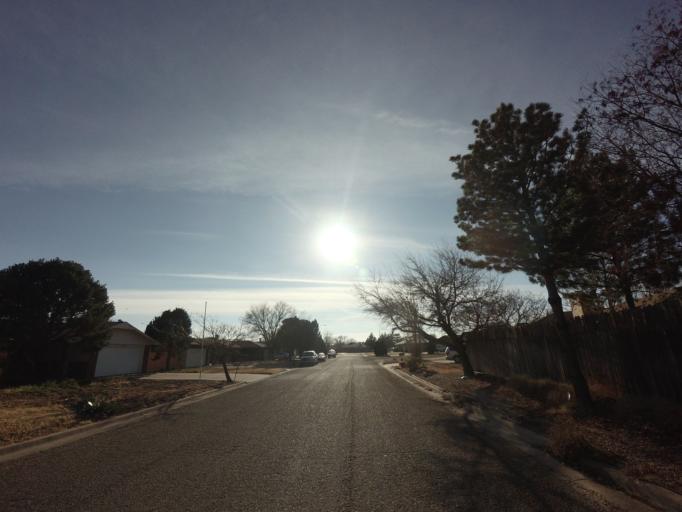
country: US
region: New Mexico
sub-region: Curry County
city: Clovis
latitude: 34.4177
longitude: -103.2270
